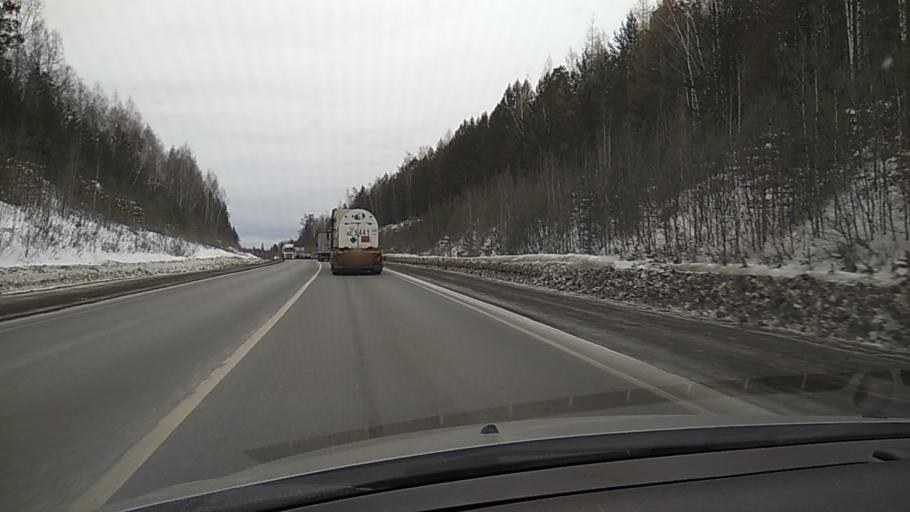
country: RU
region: Sverdlovsk
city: Talitsa
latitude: 56.8411
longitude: 60.0075
